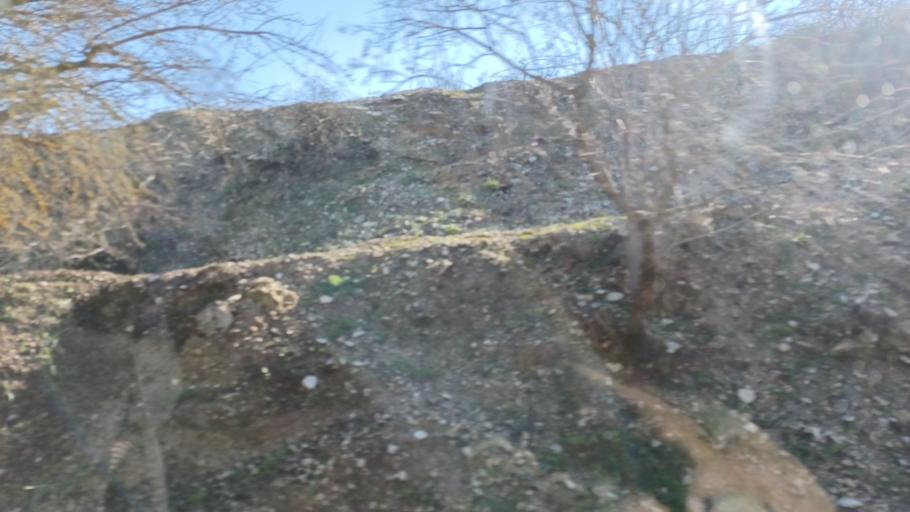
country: CY
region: Limassol
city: Pachna
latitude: 34.8120
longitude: 32.6634
